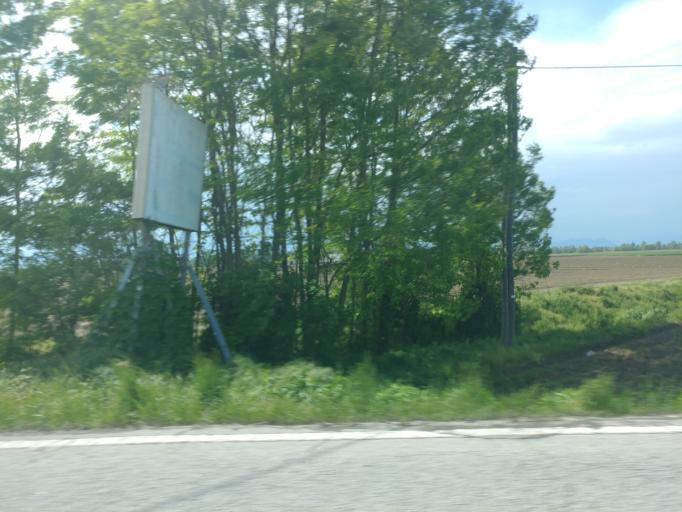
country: IT
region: Piedmont
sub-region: Provincia di Cuneo
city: Faule
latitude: 44.7868
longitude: 7.5646
